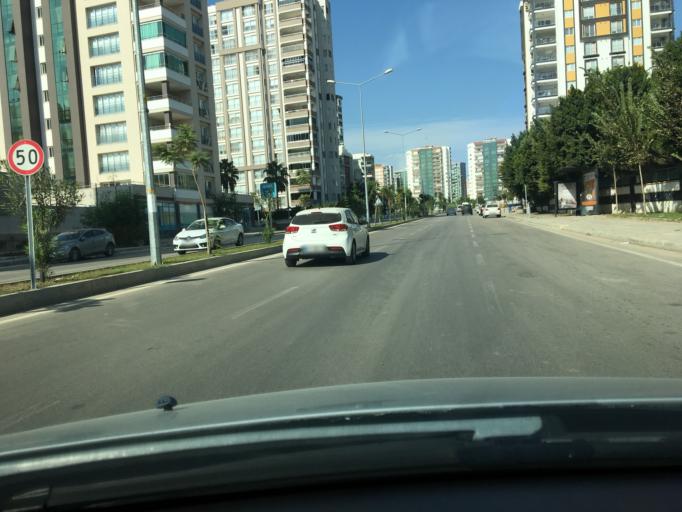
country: TR
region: Adana
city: Seyhan
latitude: 37.0200
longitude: 35.2584
